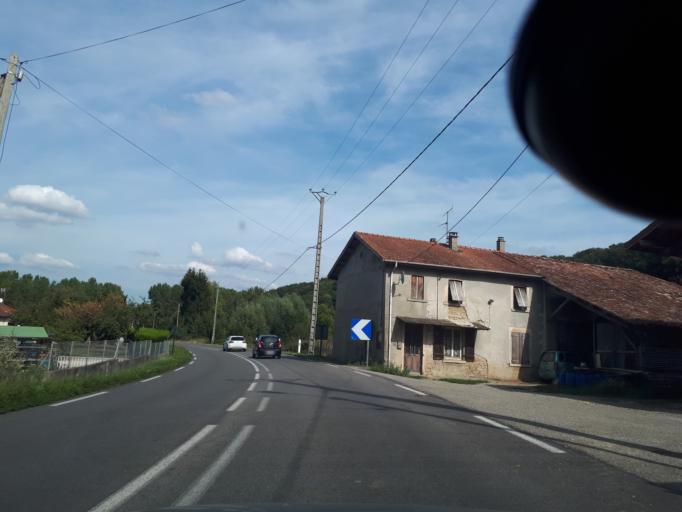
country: FR
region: Rhone-Alpes
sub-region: Departement de l'Isere
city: Maubec
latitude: 45.5489
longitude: 5.2608
